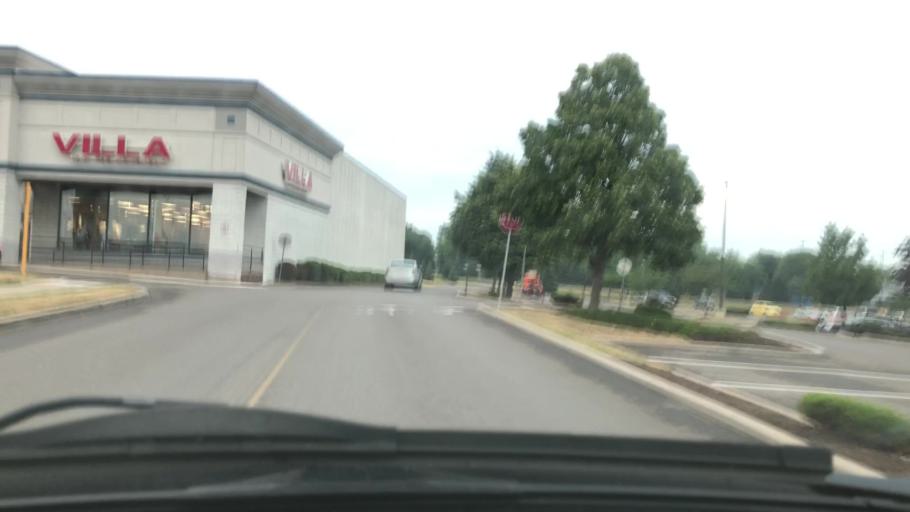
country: US
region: New York
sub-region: Erie County
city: Sloan
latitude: 42.9039
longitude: -78.7793
